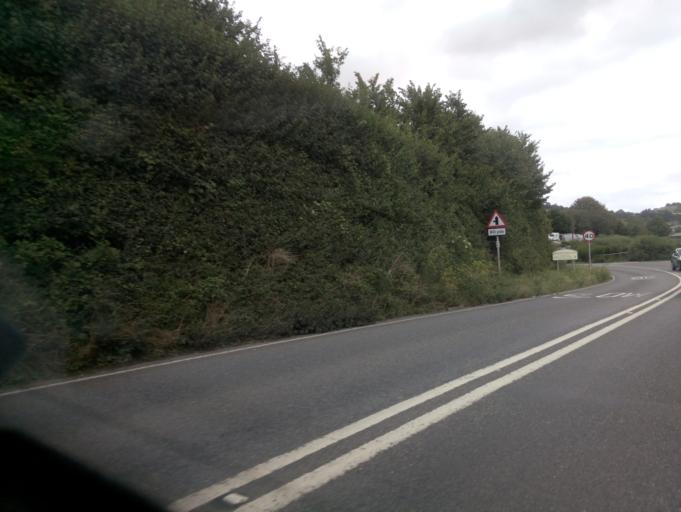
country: GB
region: England
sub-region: Devon
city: Kingsteignton
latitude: 50.5493
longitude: -3.5651
